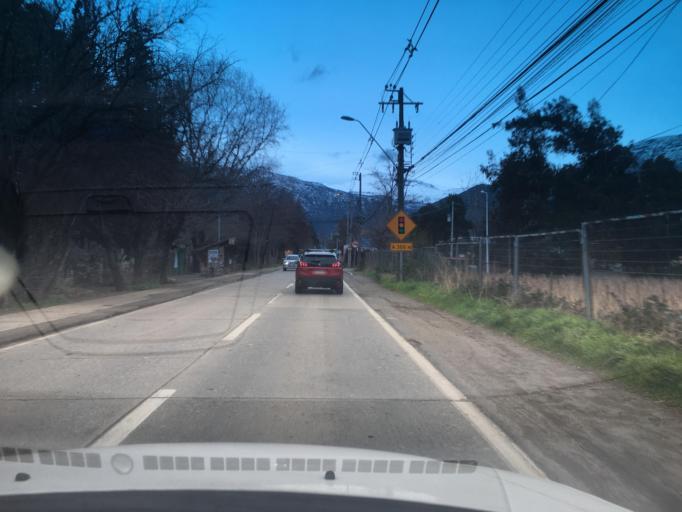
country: CL
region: Santiago Metropolitan
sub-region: Provincia de Cordillera
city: Puente Alto
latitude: -33.5829
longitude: -70.3991
